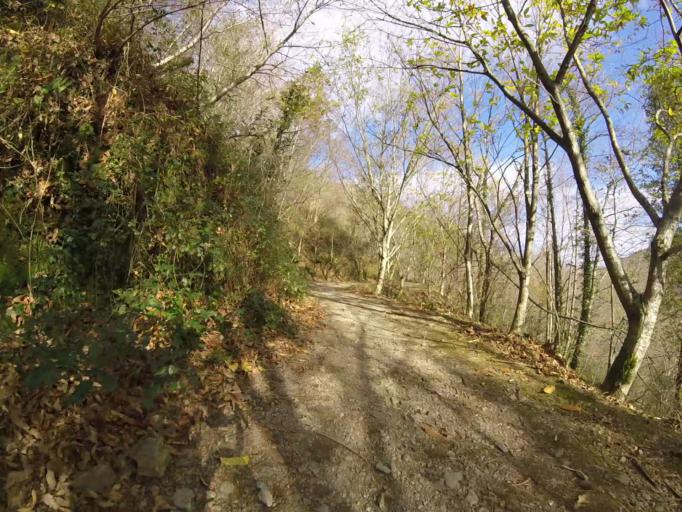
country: ES
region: Navarre
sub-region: Provincia de Navarra
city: Arano
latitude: 43.2441
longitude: -1.8673
